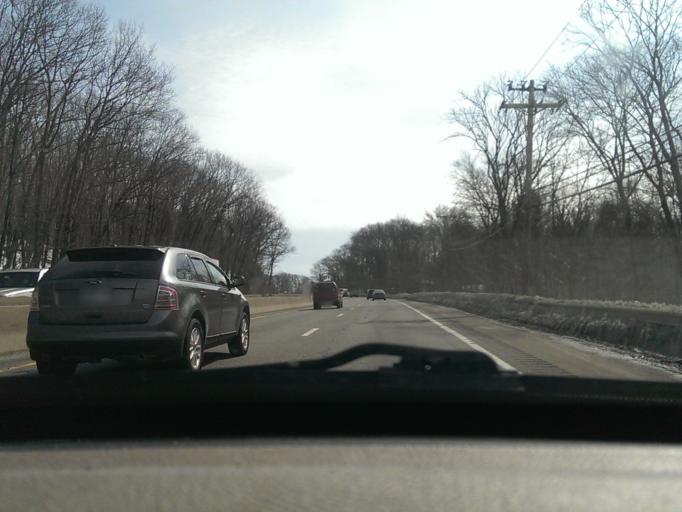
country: US
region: Massachusetts
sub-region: Worcester County
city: Millbury
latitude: 42.1833
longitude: -71.7628
